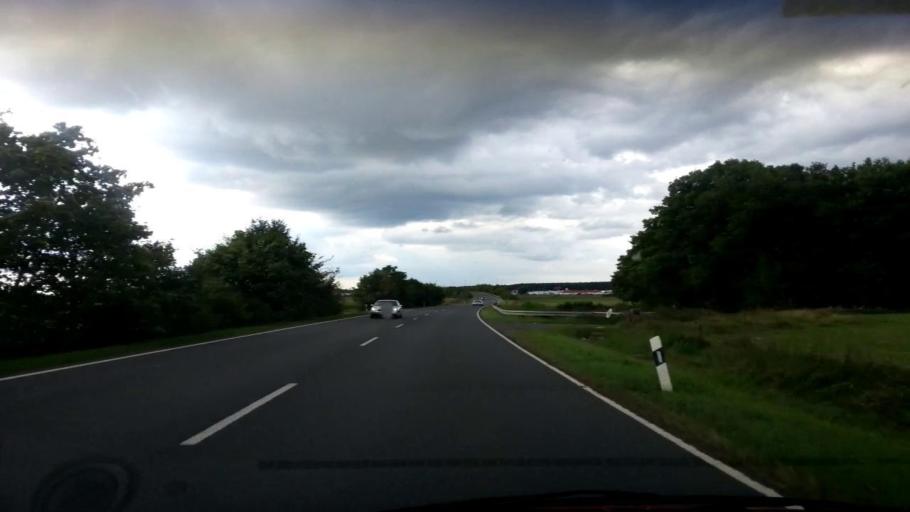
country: DE
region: Bavaria
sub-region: Regierungsbezirk Mittelfranken
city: Adelsdorf
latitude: 49.7006
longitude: 10.8918
